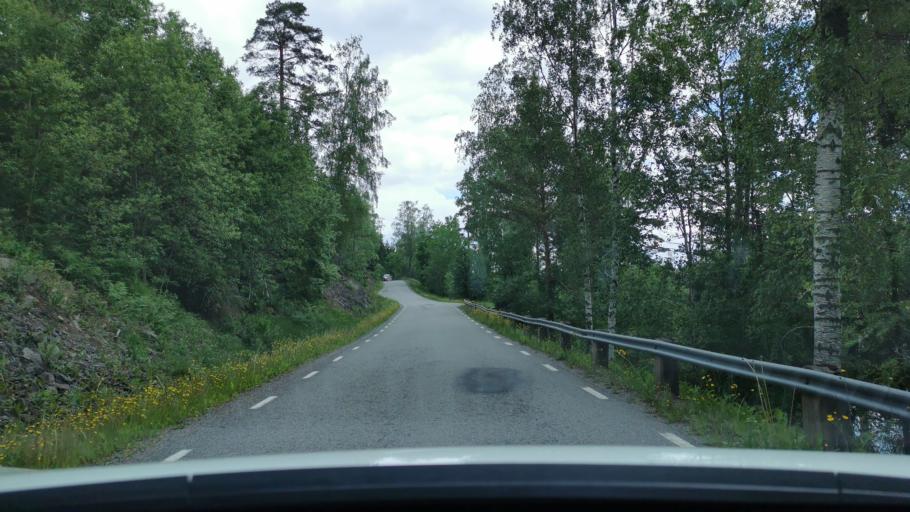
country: SE
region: Vaestra Goetaland
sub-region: Bengtsfors Kommun
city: Dals Langed
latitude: 58.8283
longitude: 12.3305
